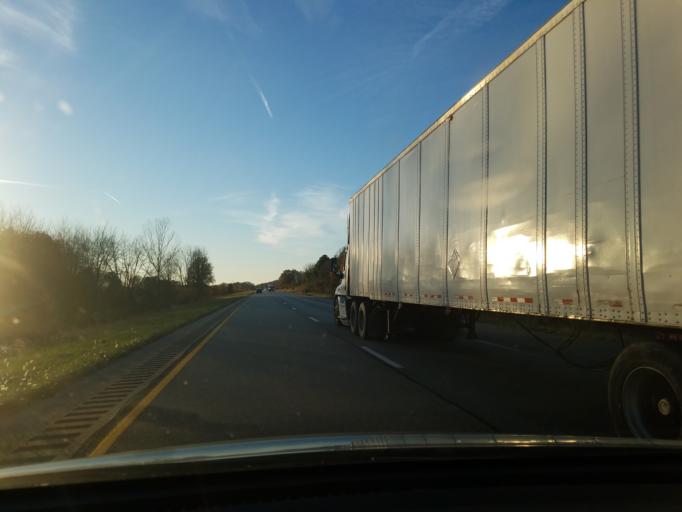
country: US
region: Indiana
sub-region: Warrick County
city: Chandler
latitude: 38.1843
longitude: -87.3710
